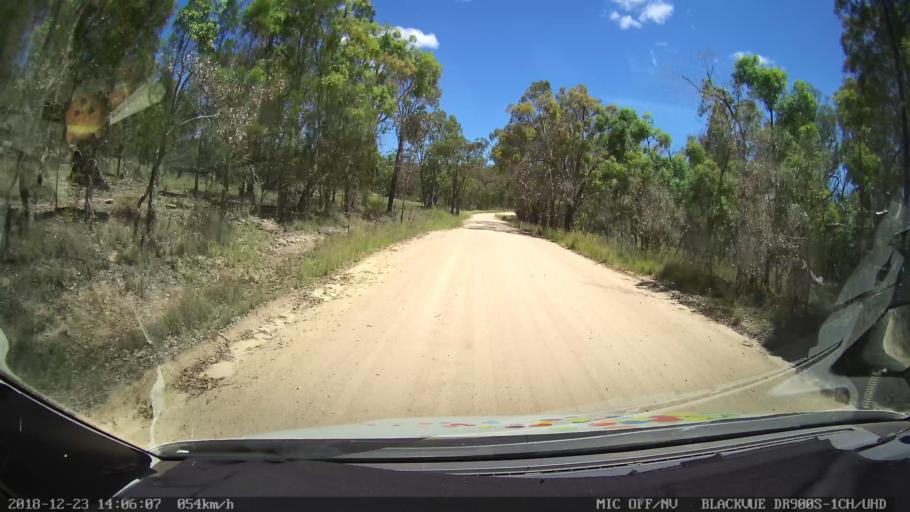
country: AU
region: New South Wales
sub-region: Tamworth Municipality
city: Manilla
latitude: -30.6284
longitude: 151.0770
